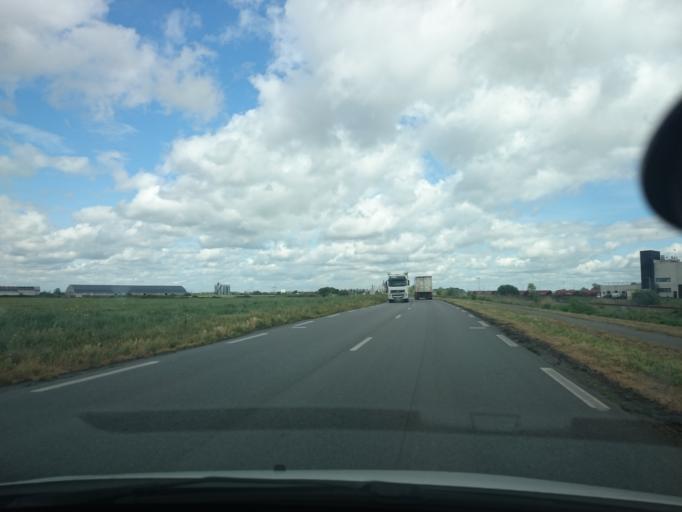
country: FR
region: Pays de la Loire
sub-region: Departement de la Loire-Atlantique
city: Montoir-de-Bretagne
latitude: 47.3149
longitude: -2.1218
